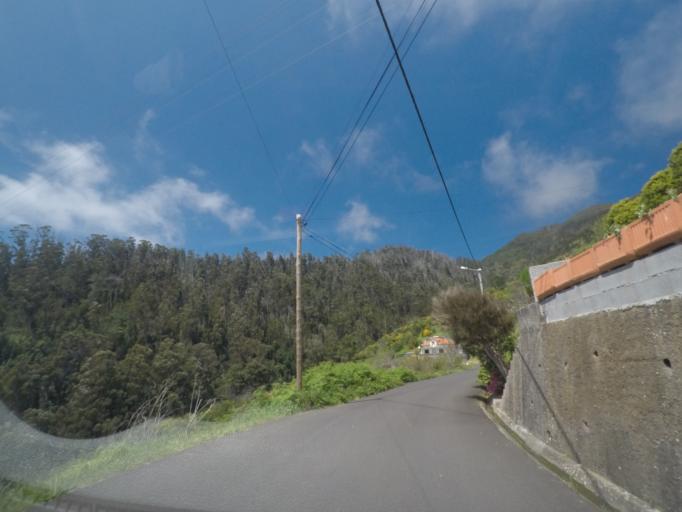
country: PT
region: Madeira
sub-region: Calheta
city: Arco da Calheta
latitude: 32.7273
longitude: -17.1289
